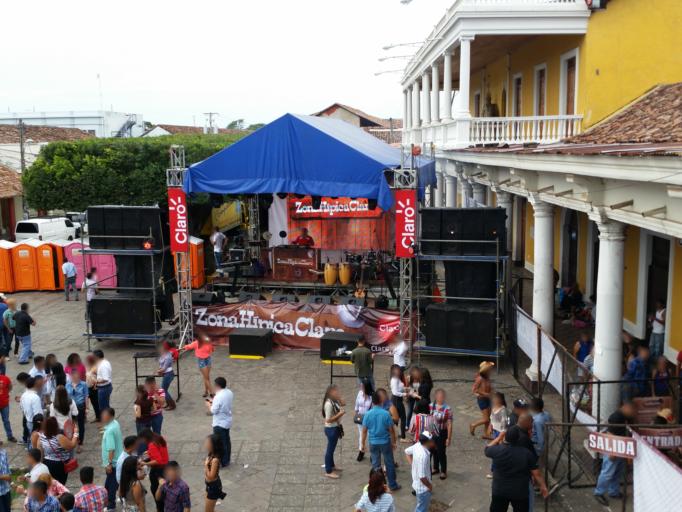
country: NI
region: Granada
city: Granada
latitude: 11.9309
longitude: -85.9535
